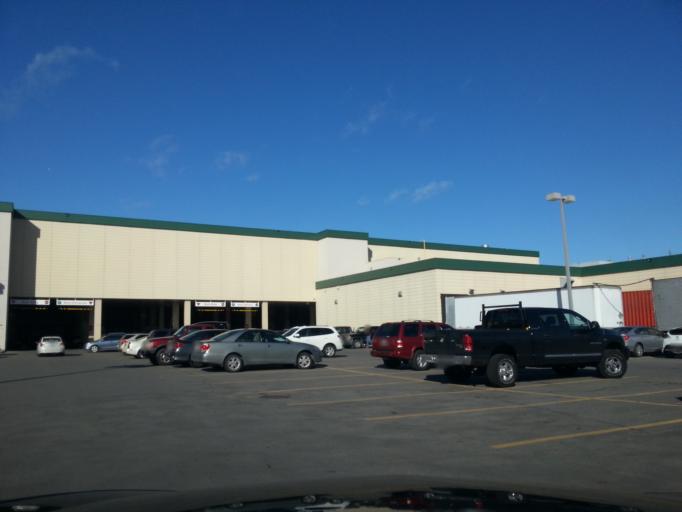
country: CA
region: Ontario
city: Ottawa
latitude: 45.3782
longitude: -75.7486
